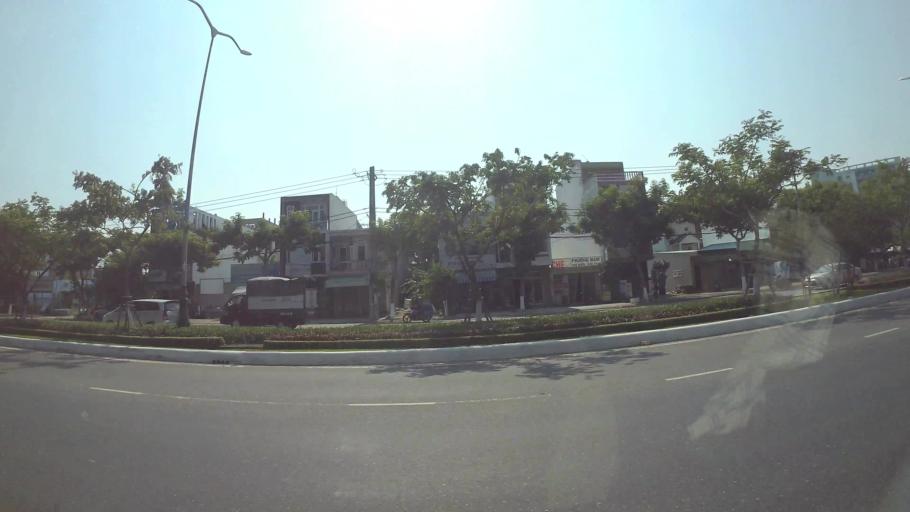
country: VN
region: Da Nang
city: Ngu Hanh Son
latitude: 16.0217
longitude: 108.2516
